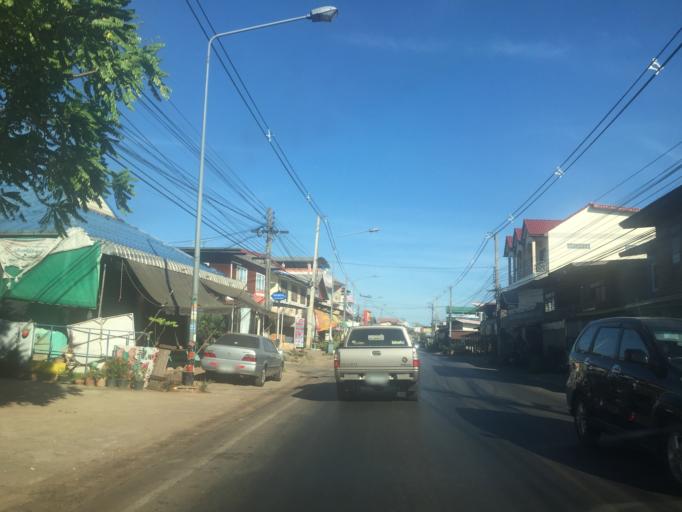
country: TH
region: Changwat Udon Thani
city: Si That
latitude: 16.9745
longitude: 103.2118
